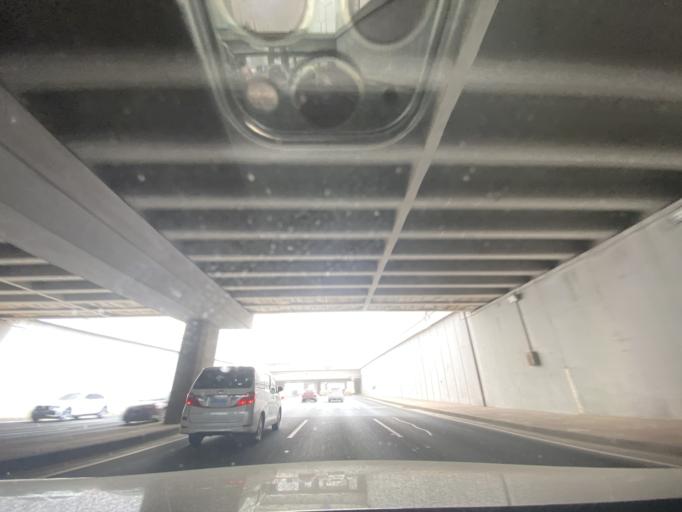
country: CN
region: Beijing
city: Jinrongjie
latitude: 39.9376
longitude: 116.3181
